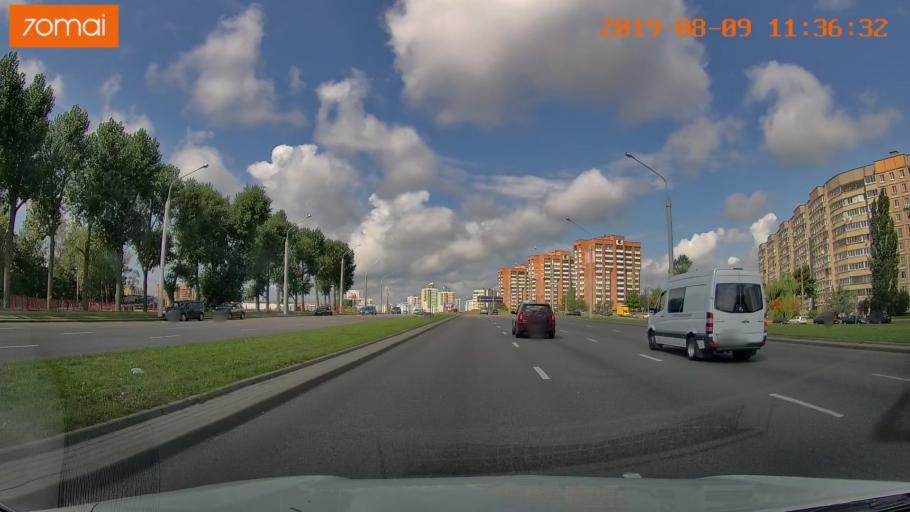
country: BY
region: Minsk
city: Novoye Medvezhino
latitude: 53.9289
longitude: 27.5007
